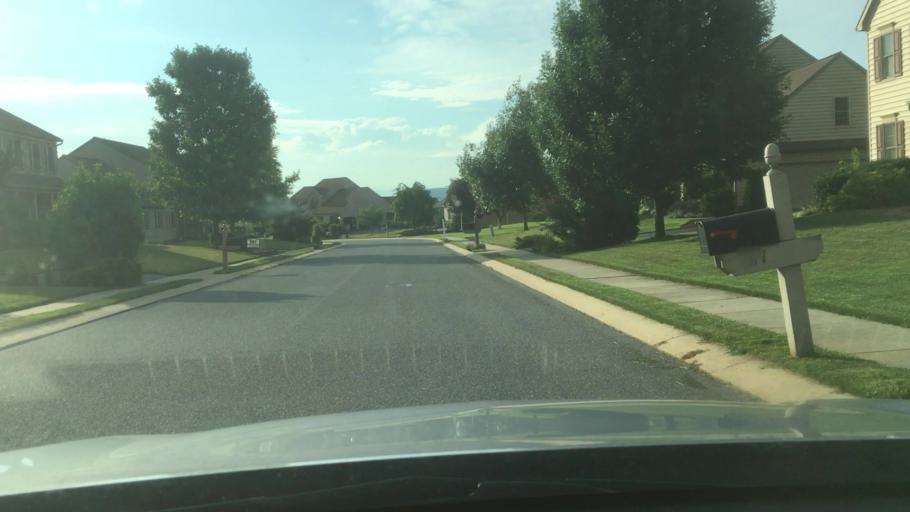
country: US
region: Pennsylvania
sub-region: York County
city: Shiloh
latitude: 39.9928
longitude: -76.7808
